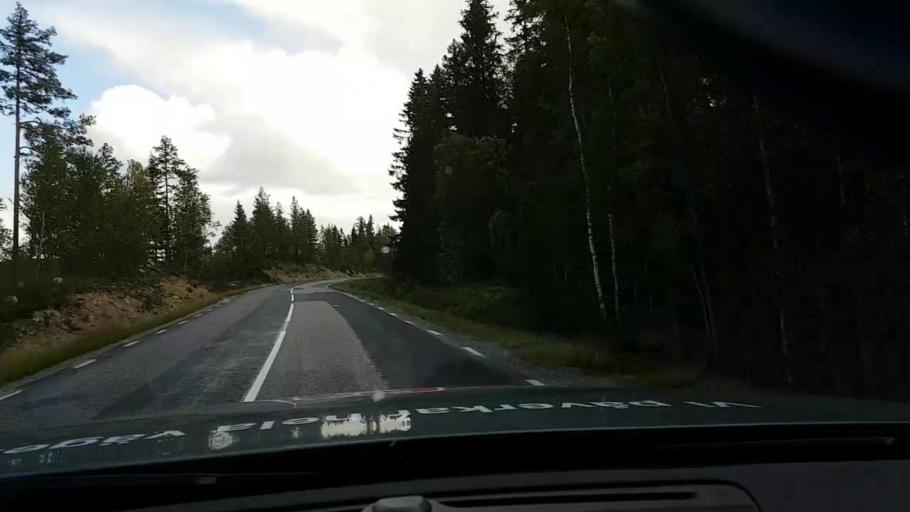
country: SE
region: Vaesterbotten
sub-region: Asele Kommun
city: Asele
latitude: 63.8341
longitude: 17.4462
